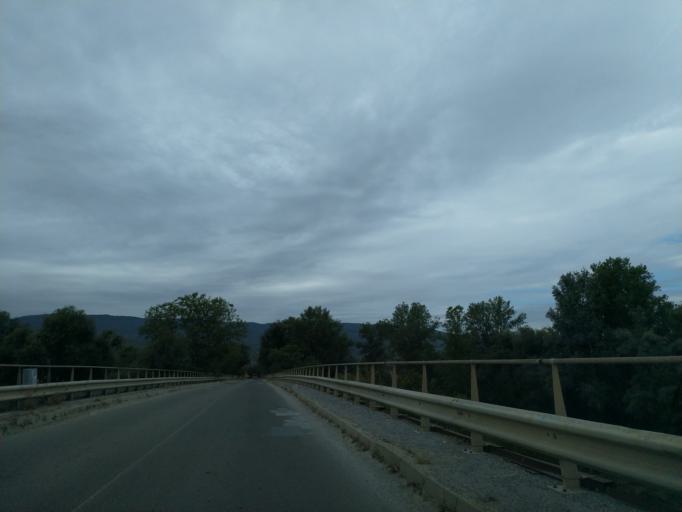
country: RS
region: Central Serbia
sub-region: Pomoravski Okrug
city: Paracin
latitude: 43.8281
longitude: 21.3454
